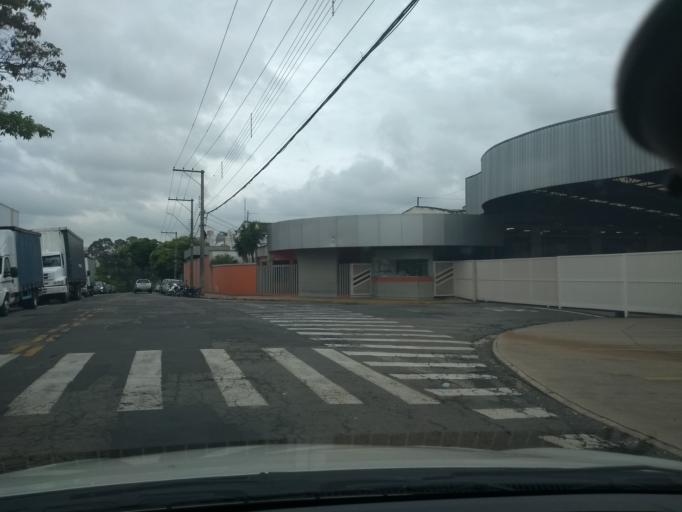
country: BR
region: Sao Paulo
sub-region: Limeira
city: Limeira
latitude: -22.5866
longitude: -47.3852
